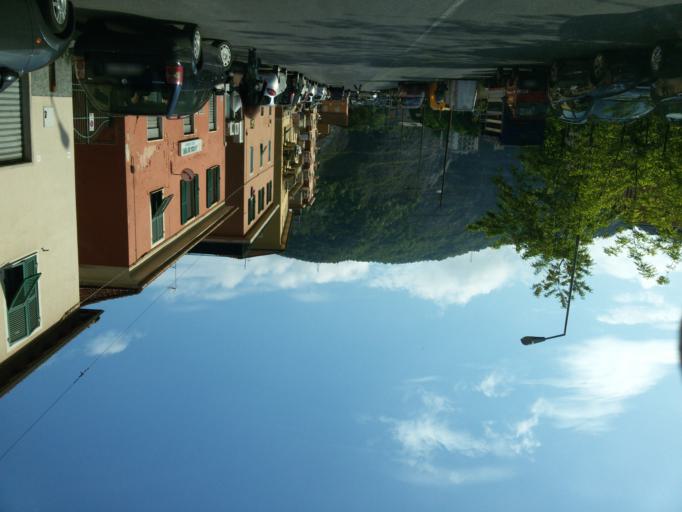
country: IT
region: Liguria
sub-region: Provincia di Genova
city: Piccarello
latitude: 44.4573
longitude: 8.9780
